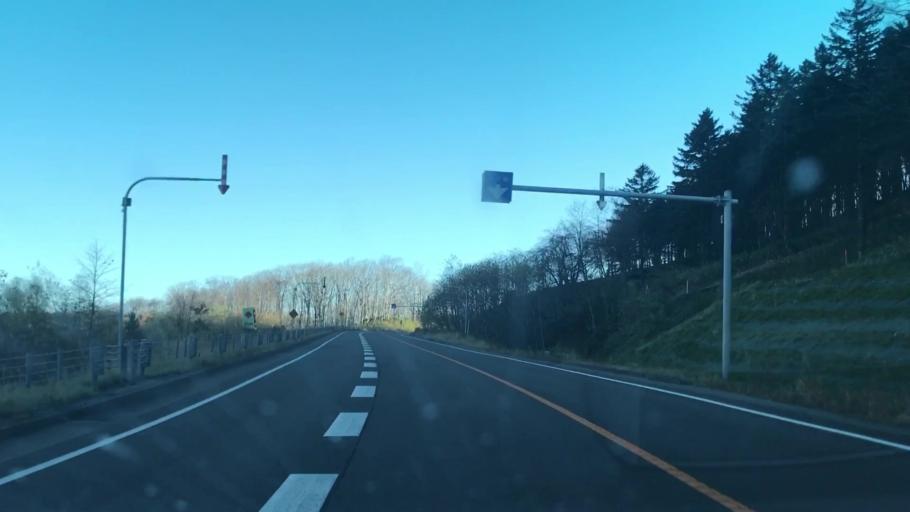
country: JP
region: Hokkaido
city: Otofuke
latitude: 42.9715
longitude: 142.8032
